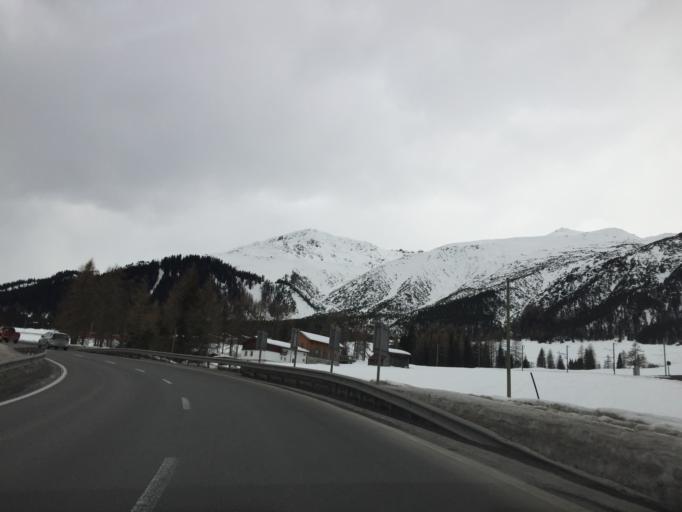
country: CH
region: Grisons
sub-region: Praettigau/Davos District
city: Davos
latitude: 46.8408
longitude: 9.8588
